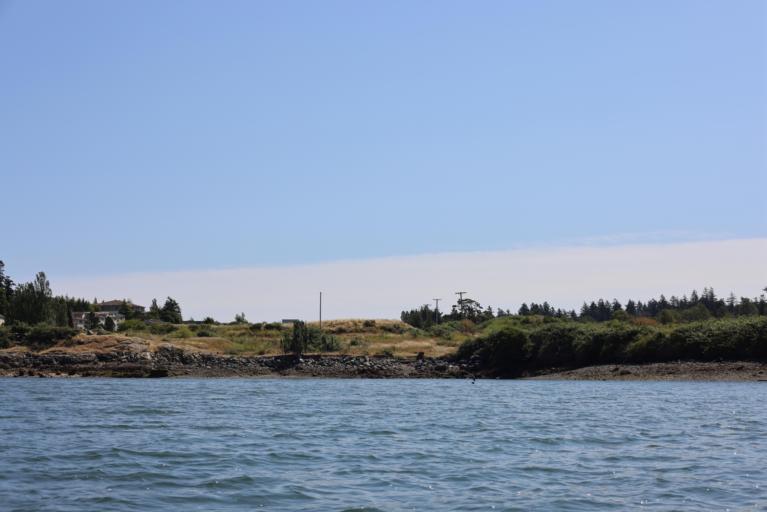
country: CA
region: British Columbia
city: Colwood
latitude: 48.4469
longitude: -123.4369
